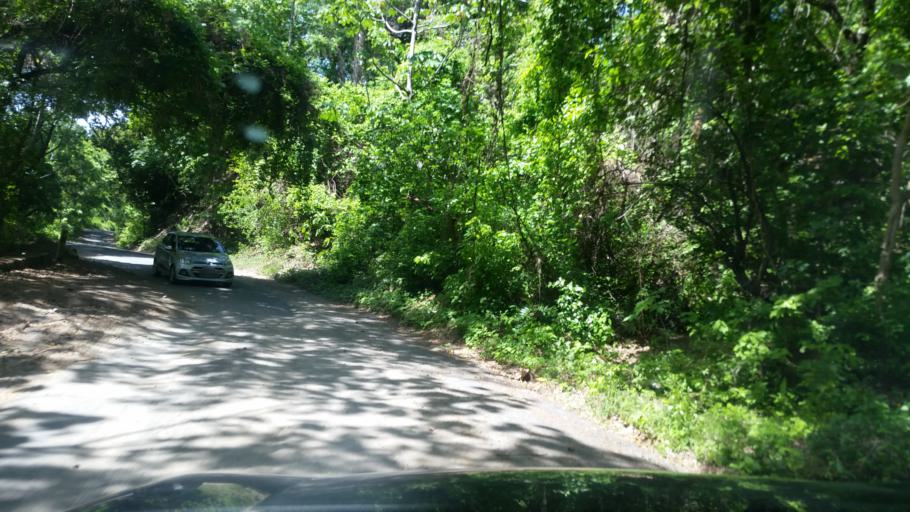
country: NI
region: Masaya
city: Catarina
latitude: 11.9348
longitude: -86.0579
